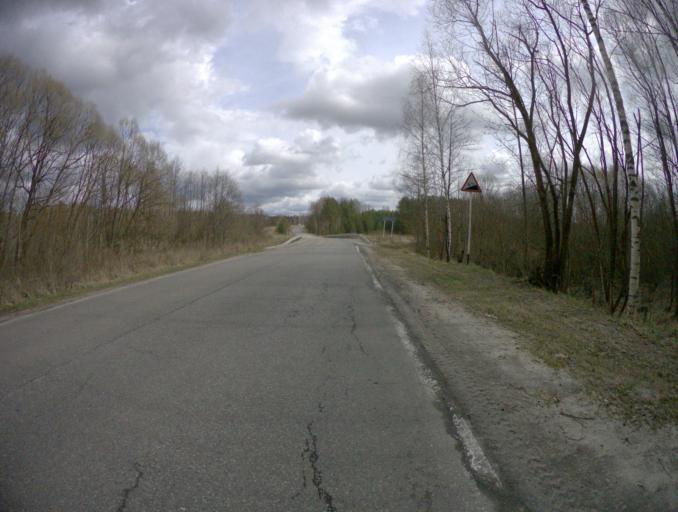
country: RU
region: Vladimir
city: Sudogda
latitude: 56.0744
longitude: 40.7779
